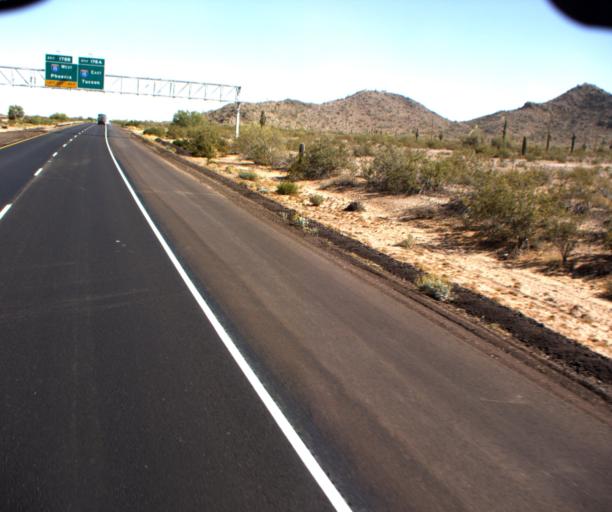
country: US
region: Arizona
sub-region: Pinal County
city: Casa Grande
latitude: 32.8325
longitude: -111.7090
